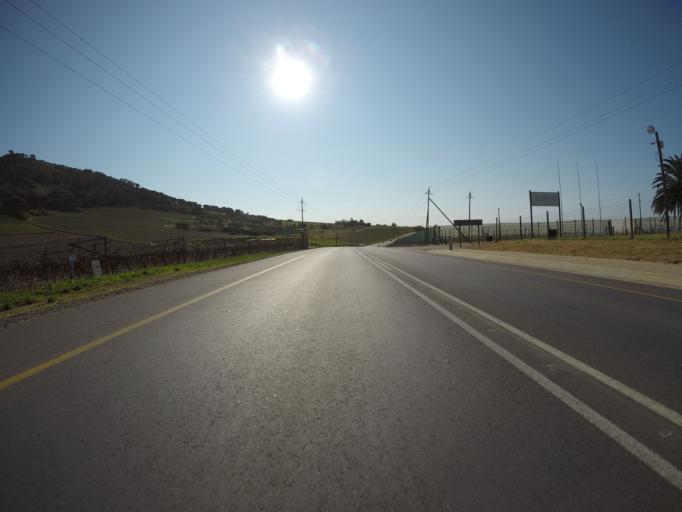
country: ZA
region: Western Cape
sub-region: Cape Winelands District Municipality
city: Noorder-Paarl
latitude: -33.6895
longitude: 18.9513
